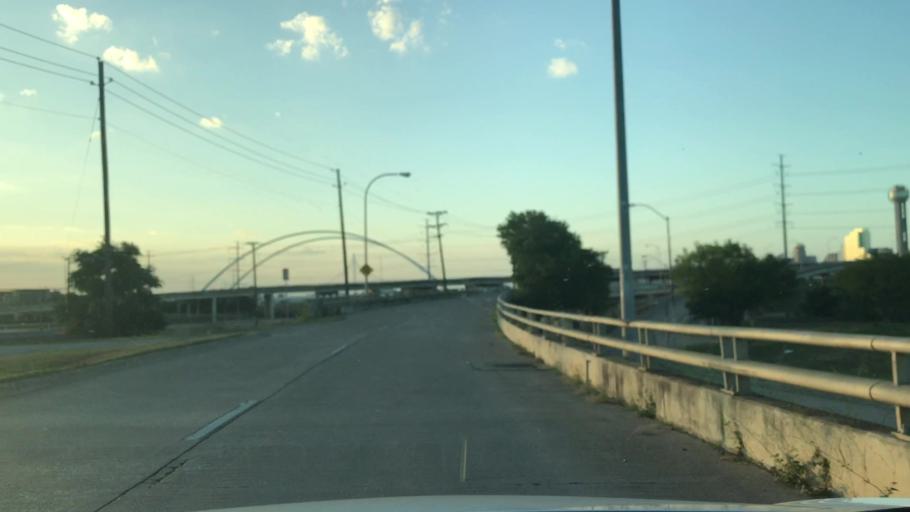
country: US
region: Texas
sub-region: Dallas County
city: Dallas
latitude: 32.7599
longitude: -96.8127
